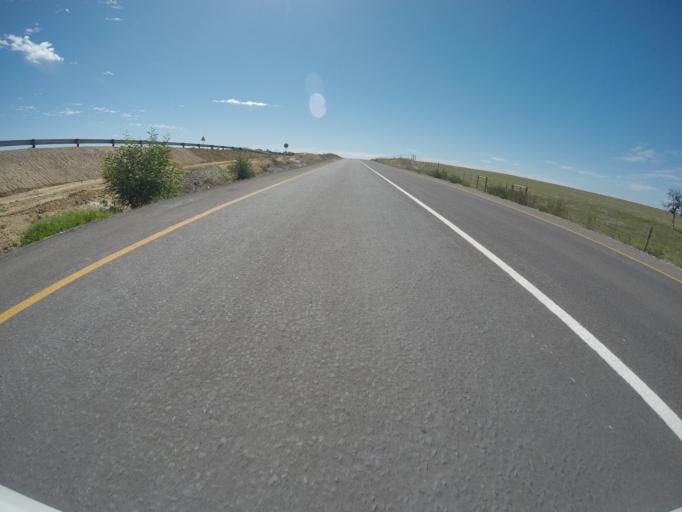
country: ZA
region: Western Cape
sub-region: West Coast District Municipality
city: Malmesbury
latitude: -33.5214
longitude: 18.6514
